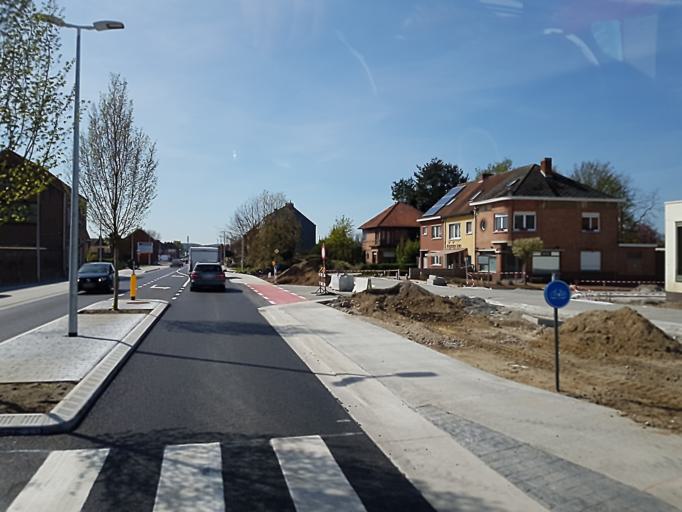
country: BE
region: Flanders
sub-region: Provincie Vlaams-Brabant
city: Aarschot
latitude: 51.0056
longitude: 4.8370
